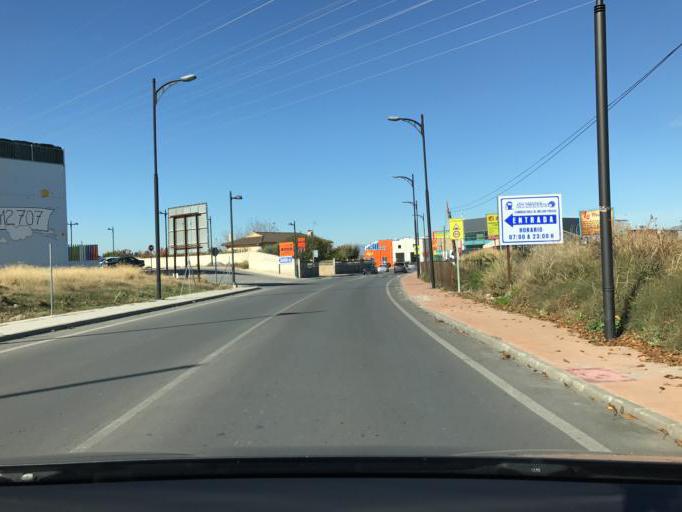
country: ES
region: Andalusia
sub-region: Provincia de Granada
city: Cullar-Vega
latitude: 37.1487
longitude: -3.6617
